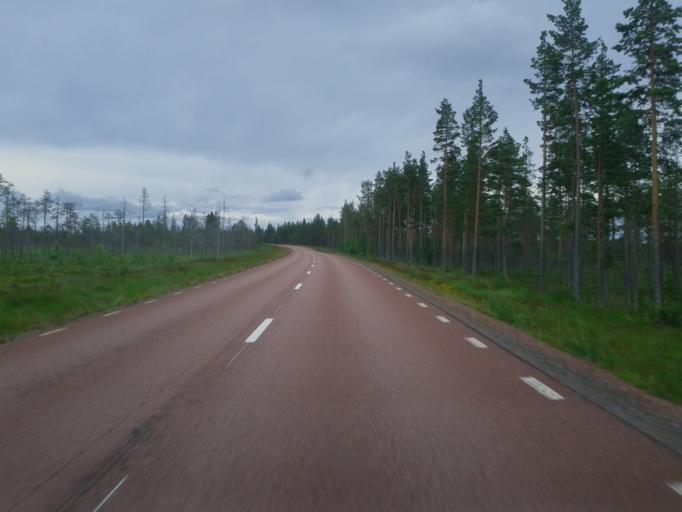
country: SE
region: Dalarna
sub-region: Alvdalens Kommun
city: AElvdalen
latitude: 61.5560
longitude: 13.3199
